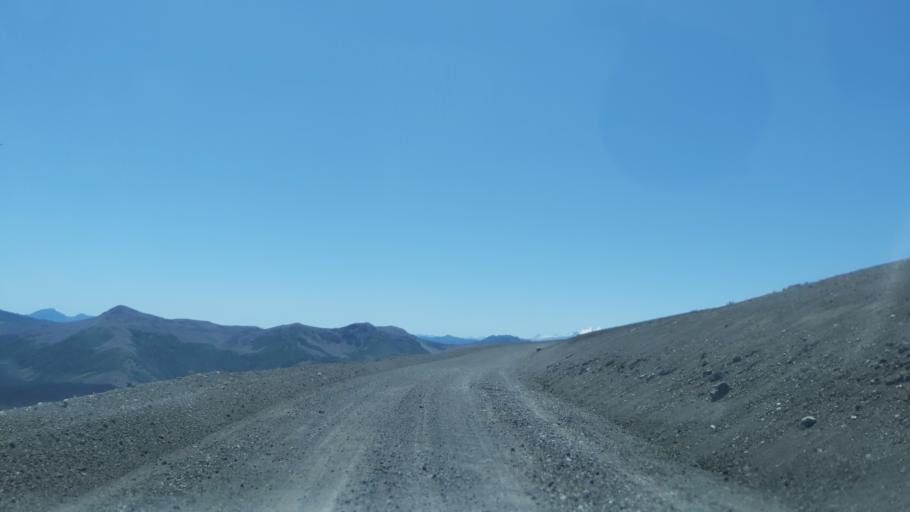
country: CL
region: Araucania
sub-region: Provincia de Cautin
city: Vilcun
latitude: -38.3692
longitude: -71.5400
